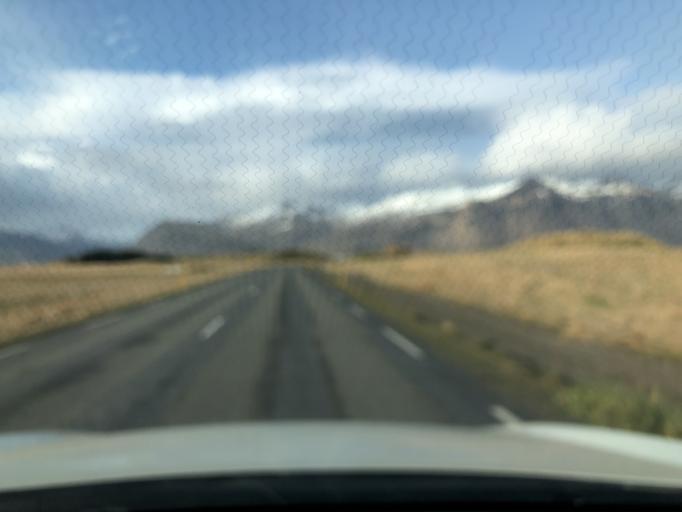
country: IS
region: East
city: Hoefn
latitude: 64.2765
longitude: -15.1997
